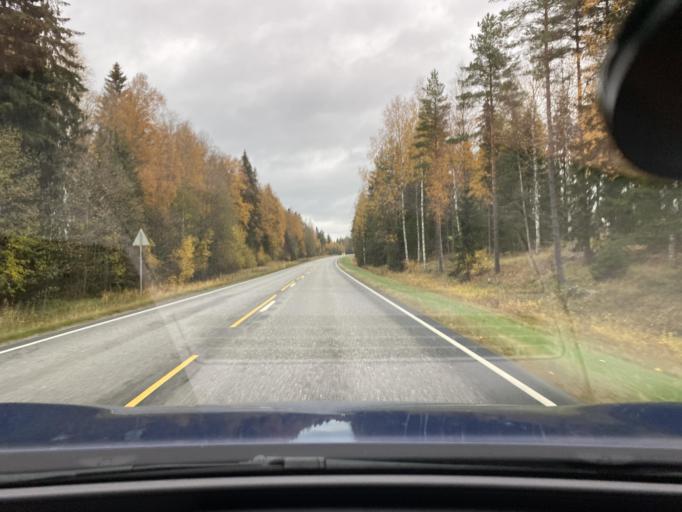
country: FI
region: Varsinais-Suomi
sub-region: Loimaa
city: Ylaene
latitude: 60.9009
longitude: 22.4069
